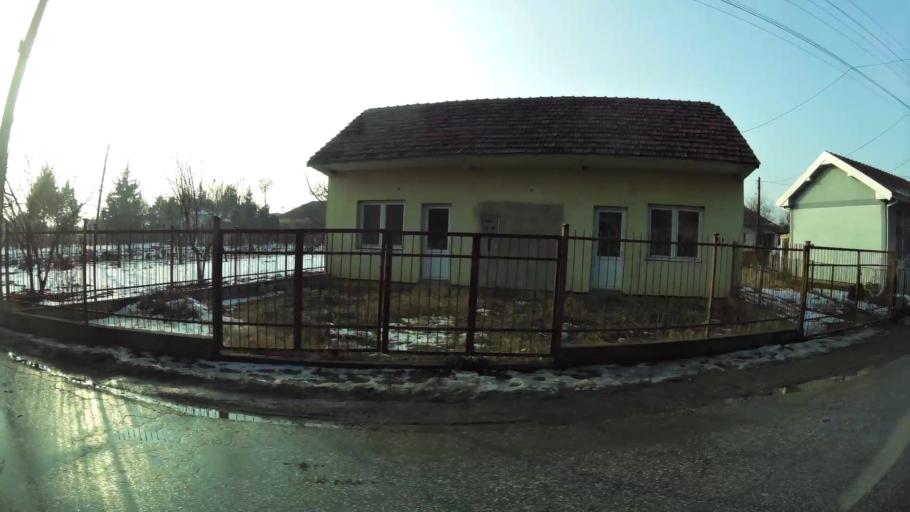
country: MK
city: Miladinovci
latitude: 41.9884
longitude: 21.6522
